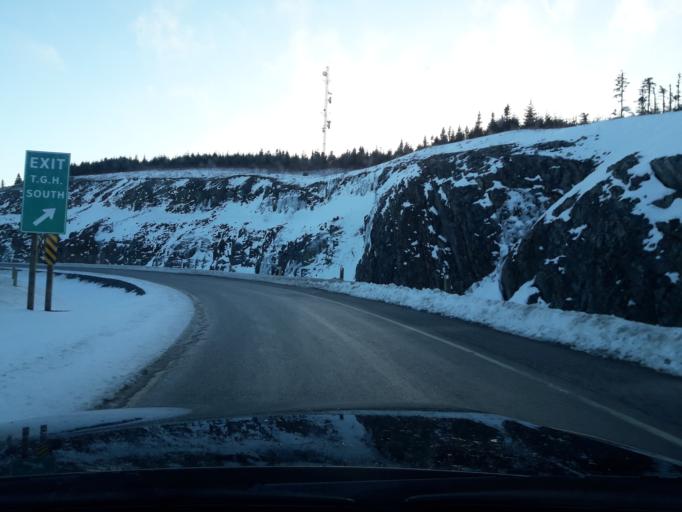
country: CA
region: Newfoundland and Labrador
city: Mount Pearl
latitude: 47.5487
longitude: -52.7662
